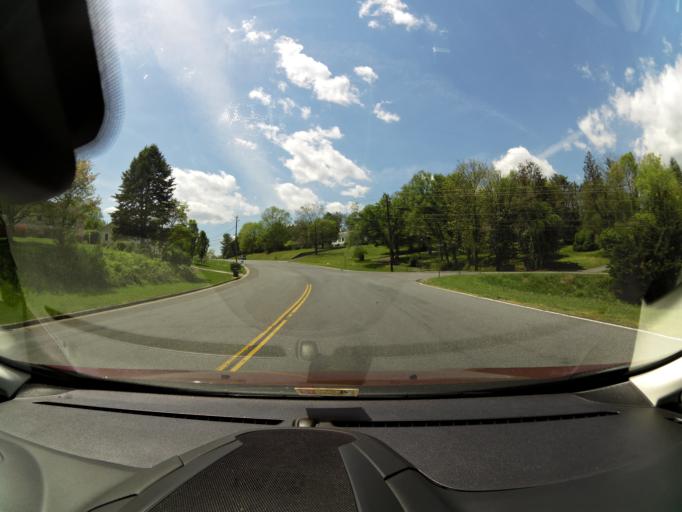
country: US
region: Virginia
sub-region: City of Lexington
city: Lexington
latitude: 37.7695
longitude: -79.4514
